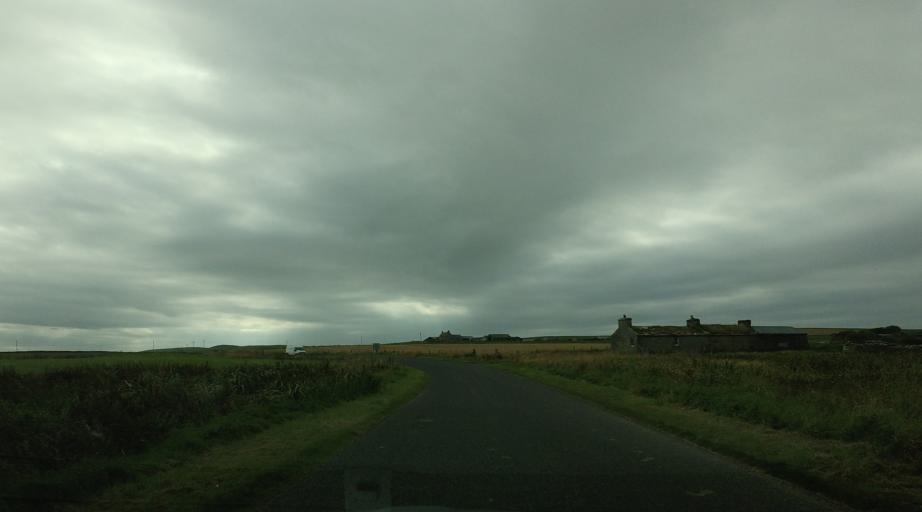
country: GB
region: Scotland
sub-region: Orkney Islands
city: Stromness
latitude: 59.0399
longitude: -3.3104
